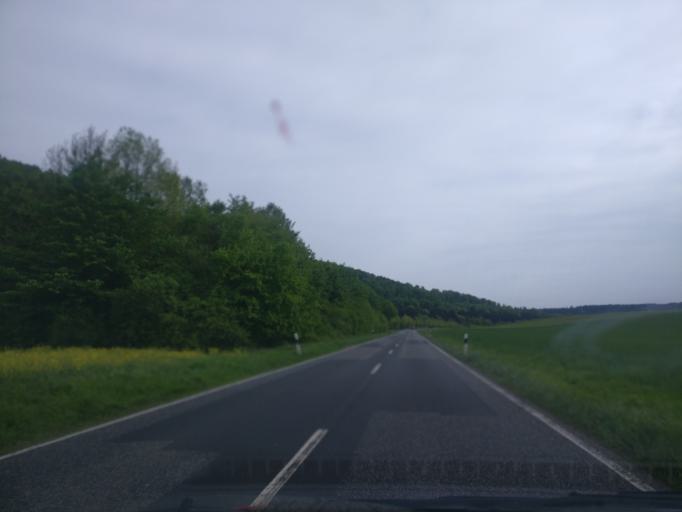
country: DE
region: Hesse
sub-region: Regierungsbezirk Kassel
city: Fuldatal
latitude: 51.3988
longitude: 9.5752
